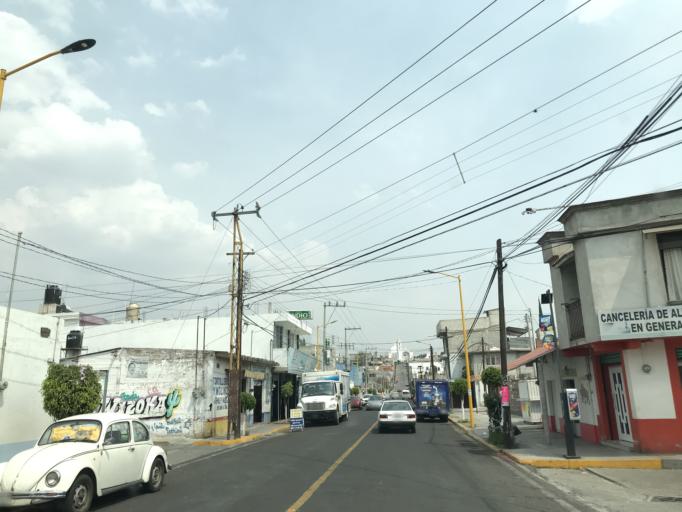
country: MX
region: Tlaxcala
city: Panotla
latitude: 19.3181
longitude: -98.2710
